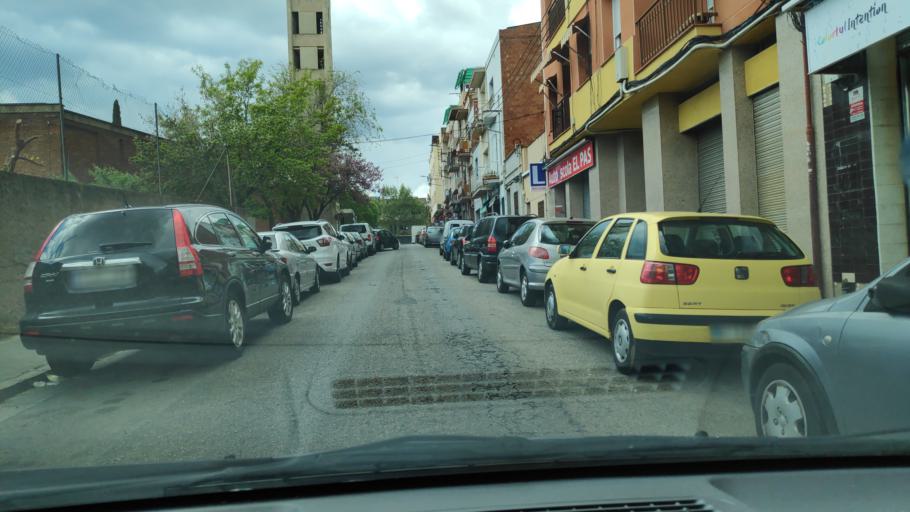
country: ES
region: Catalonia
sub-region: Provincia de Barcelona
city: Sabadell
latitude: 41.5643
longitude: 2.0919
